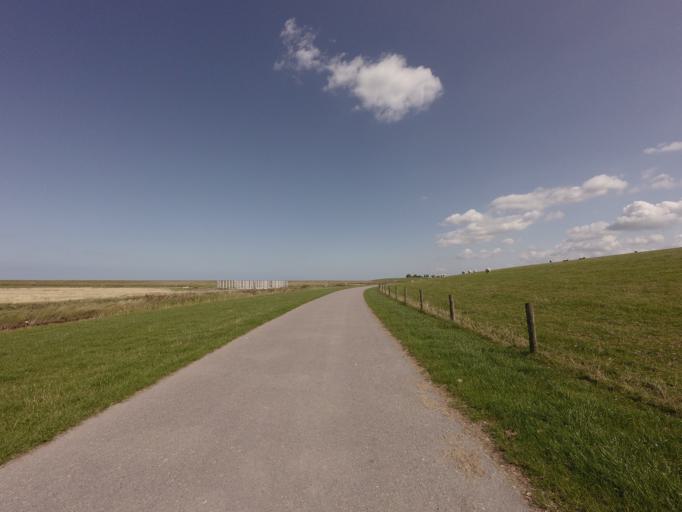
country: NL
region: Friesland
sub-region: Gemeente Ferwerderadiel
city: Marrum
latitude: 53.3378
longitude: 5.7838
